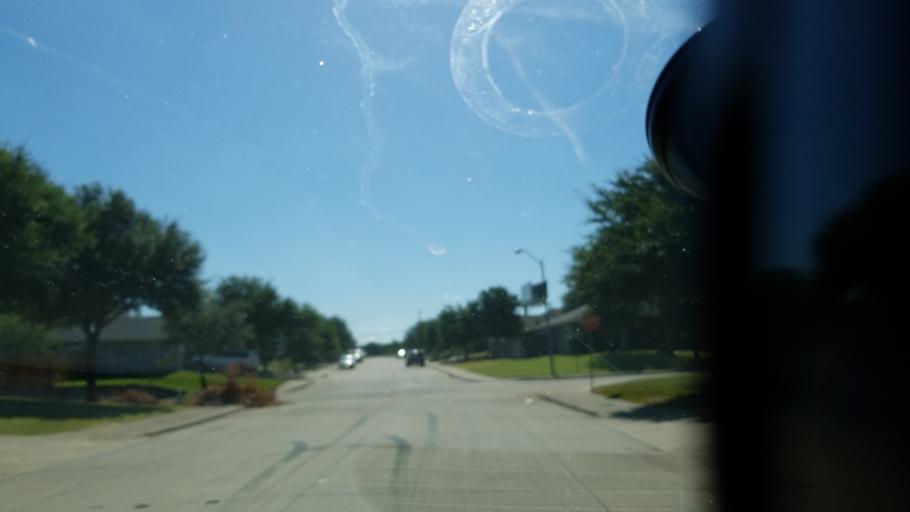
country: US
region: Texas
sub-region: Dallas County
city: Cockrell Hill
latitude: 32.6776
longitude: -96.8250
